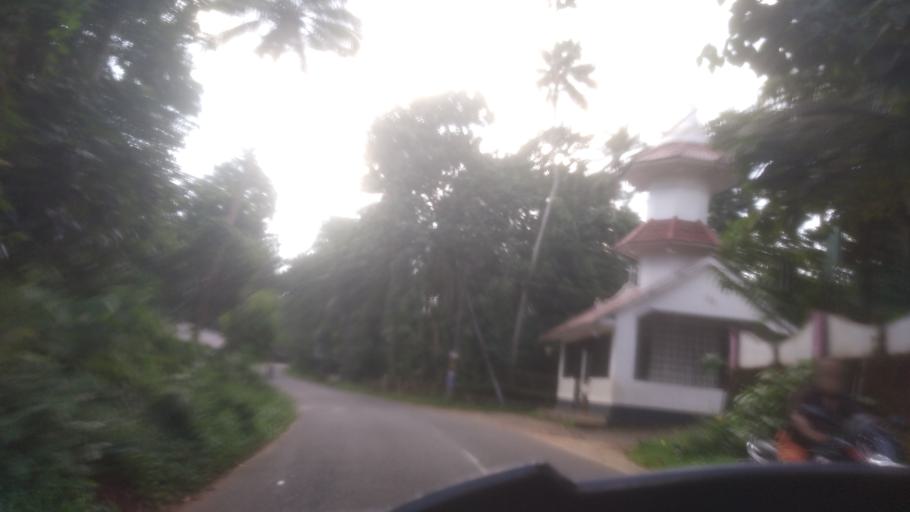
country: IN
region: Kerala
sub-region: Ernakulam
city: Kotamangalam
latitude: 10.0045
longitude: 76.6562
